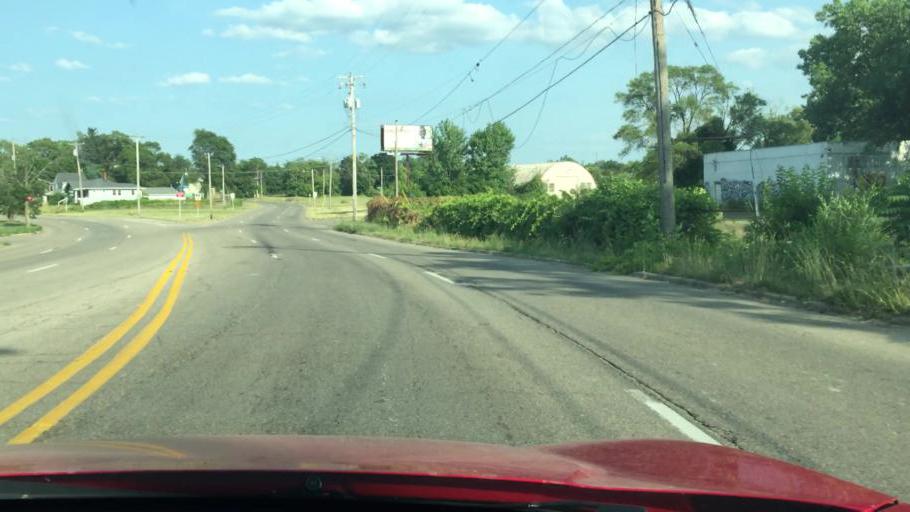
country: US
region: Michigan
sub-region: Genesee County
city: Flint
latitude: 43.0344
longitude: -83.6821
